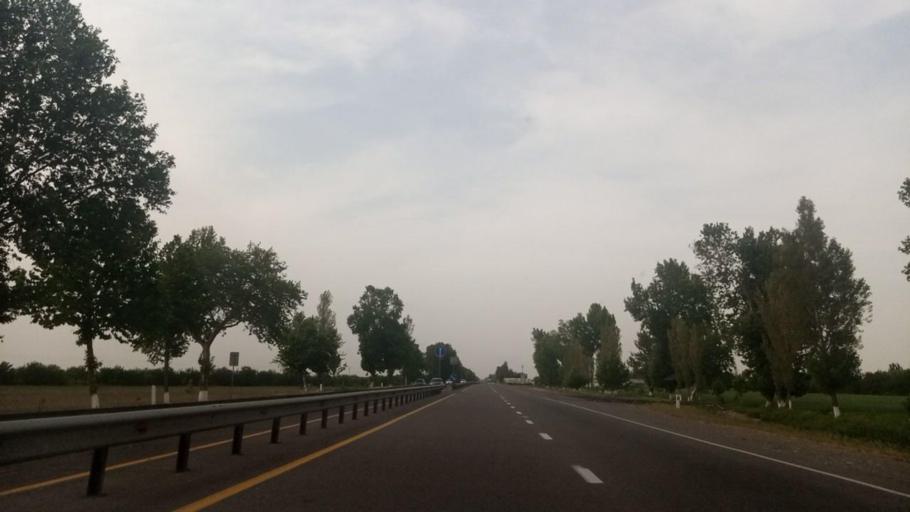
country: UZ
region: Toshkent Shahri
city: Bektemir
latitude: 41.2039
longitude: 69.4030
